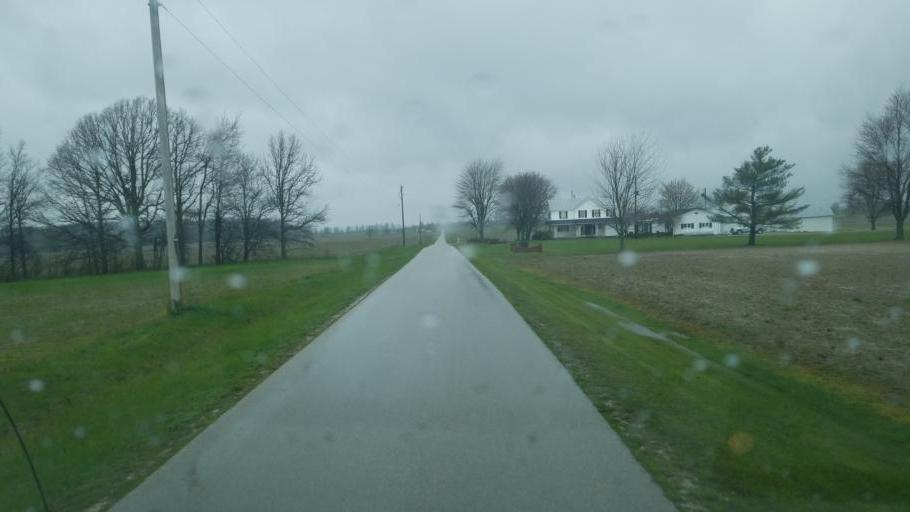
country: US
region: Ohio
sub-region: Hardin County
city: Forest
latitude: 40.7700
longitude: -83.4777
